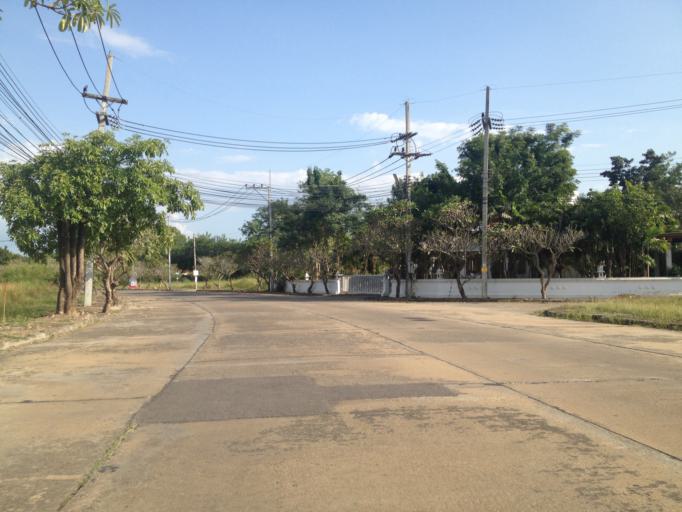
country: TH
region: Chiang Mai
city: Hang Dong
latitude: 18.6979
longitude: 98.9367
